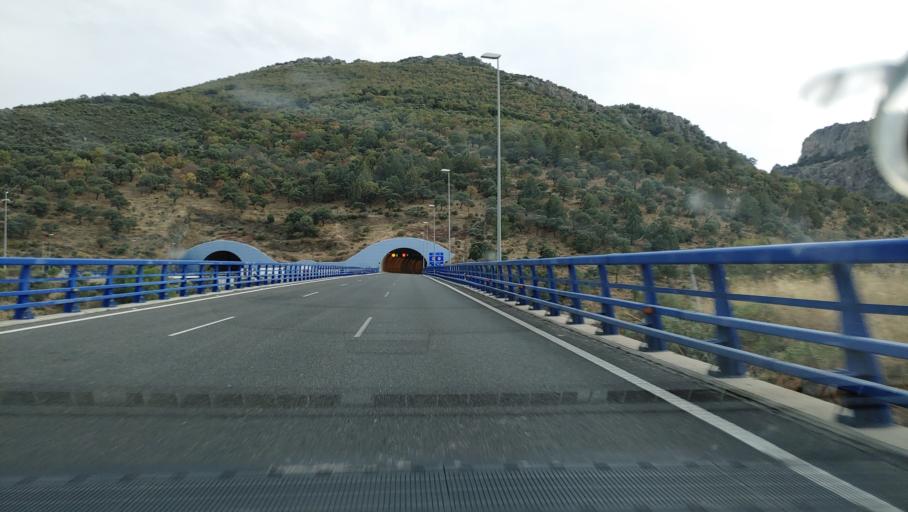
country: ES
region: Andalusia
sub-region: Provincia de Jaen
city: Santa Elena
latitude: 38.4016
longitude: -3.4995
